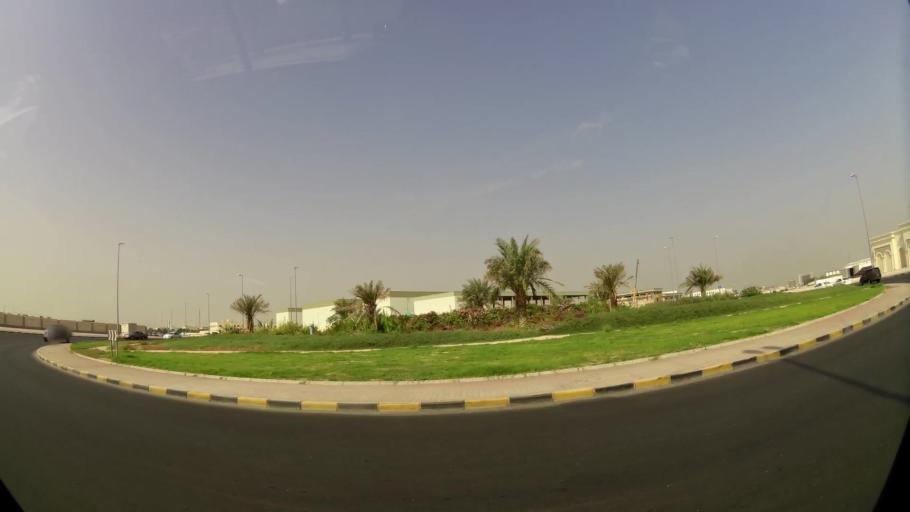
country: KW
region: Al Asimah
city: Ar Rabiyah
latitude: 29.2790
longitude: 47.9153
